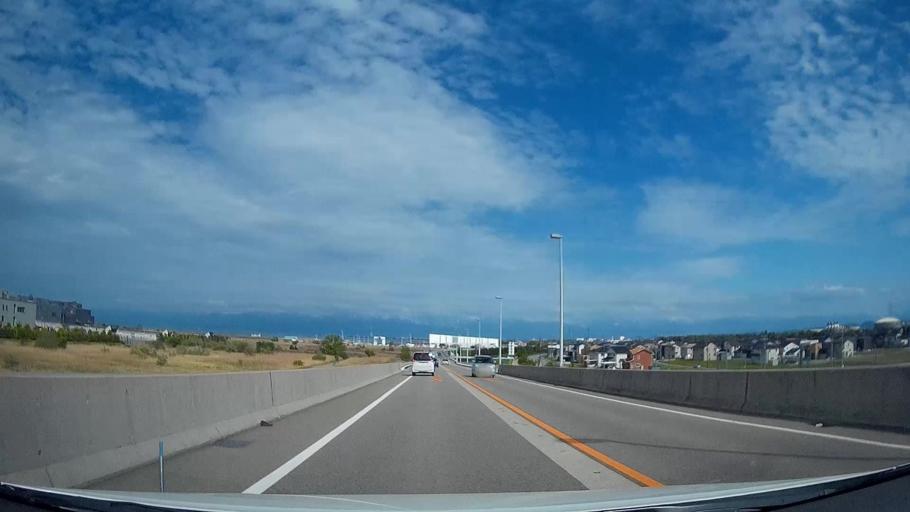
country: JP
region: Toyama
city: Kuragaki-kosugi
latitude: 36.7740
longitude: 137.1277
